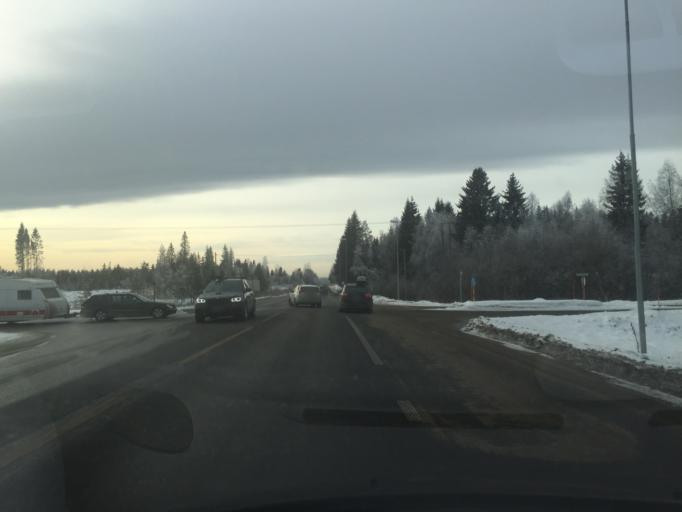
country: NO
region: Hedmark
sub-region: Elverum
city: Elverum
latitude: 60.9325
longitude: 11.6747
